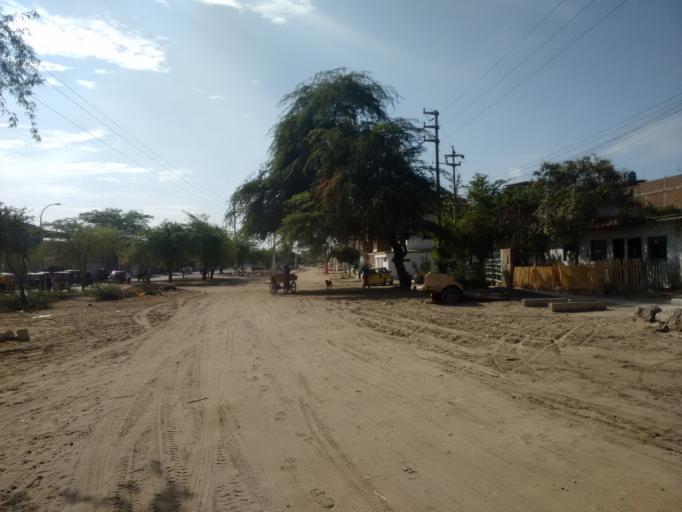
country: PE
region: Piura
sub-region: Provincia de Piura
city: Piura
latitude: -5.1741
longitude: -80.6437
